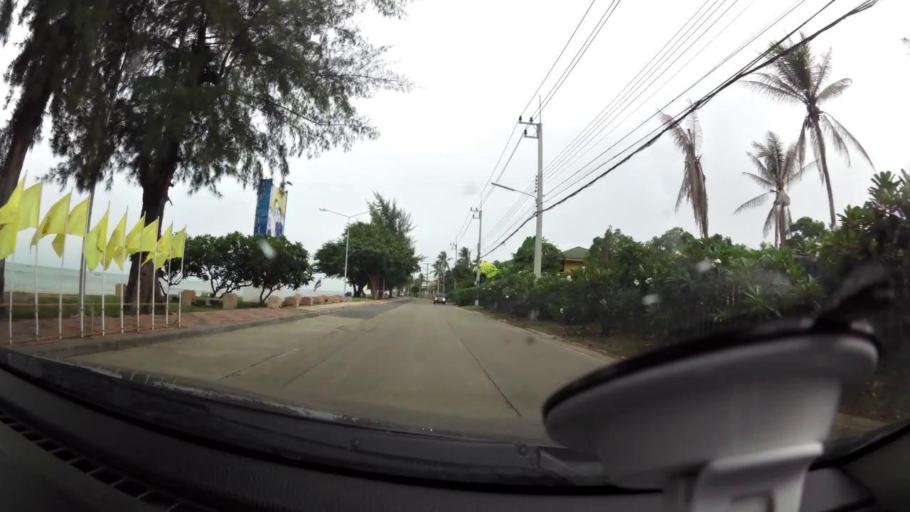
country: TH
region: Prachuap Khiri Khan
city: Pran Buri
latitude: 12.3969
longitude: 99.9951
